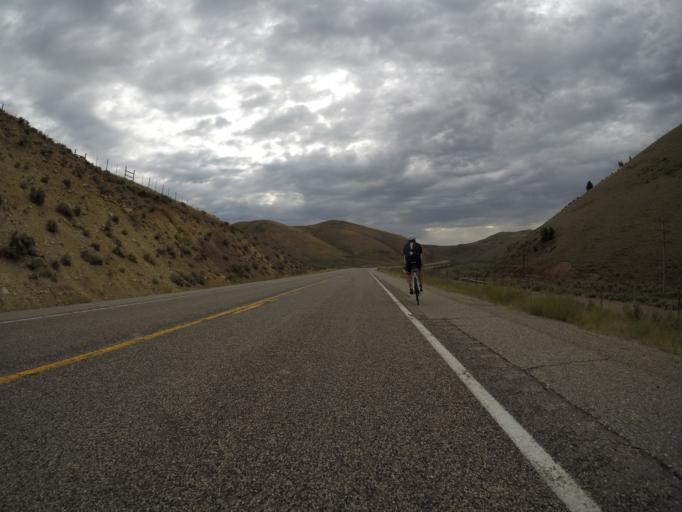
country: US
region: Wyoming
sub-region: Lincoln County
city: Kemmerer
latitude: 41.8251
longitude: -110.8452
